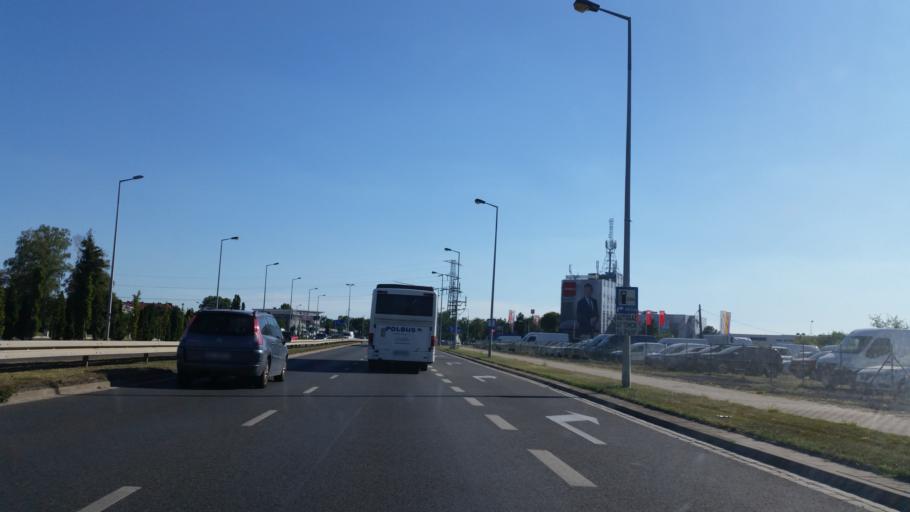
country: PL
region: Lower Silesian Voivodeship
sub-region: Powiat wroclawski
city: Bielany Wroclawskie
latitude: 51.0656
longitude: 17.0027
